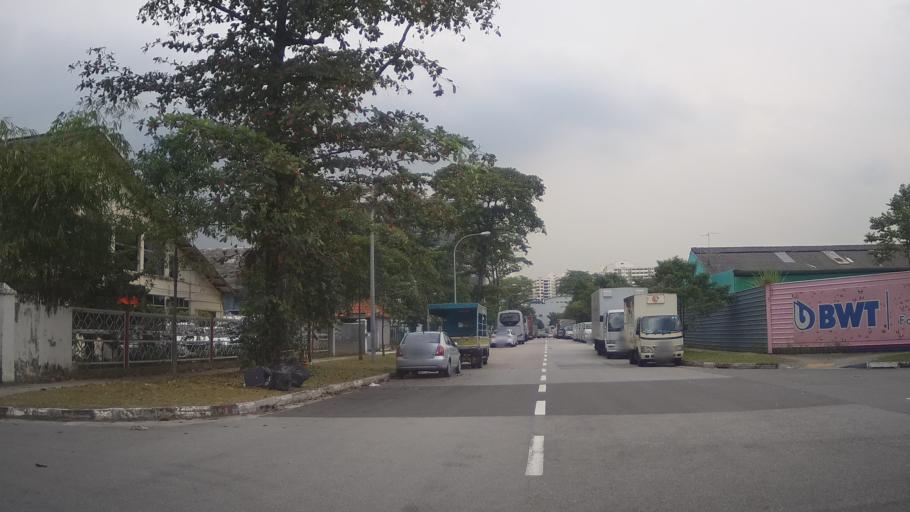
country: MY
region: Johor
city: Johor Bahru
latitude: 1.3301
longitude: 103.7037
